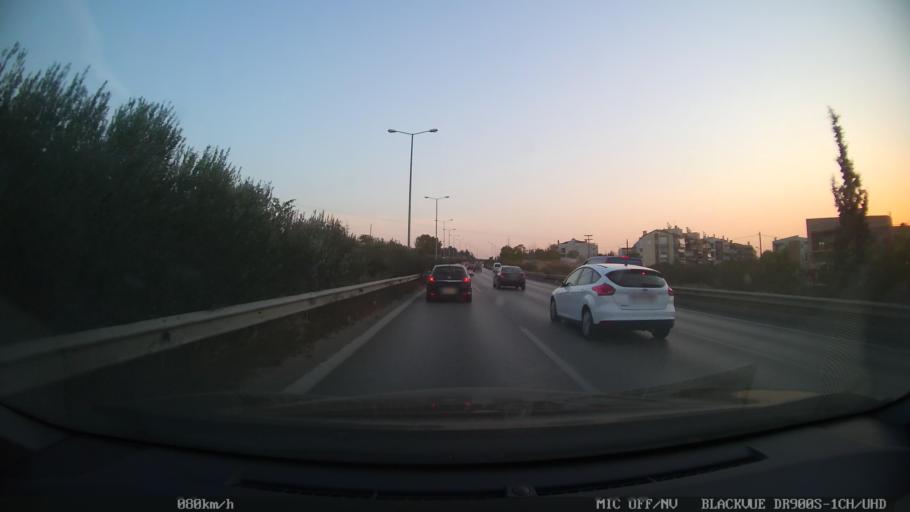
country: GR
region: Central Macedonia
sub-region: Nomos Thessalonikis
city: Pylaia
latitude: 40.6037
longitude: 22.9987
